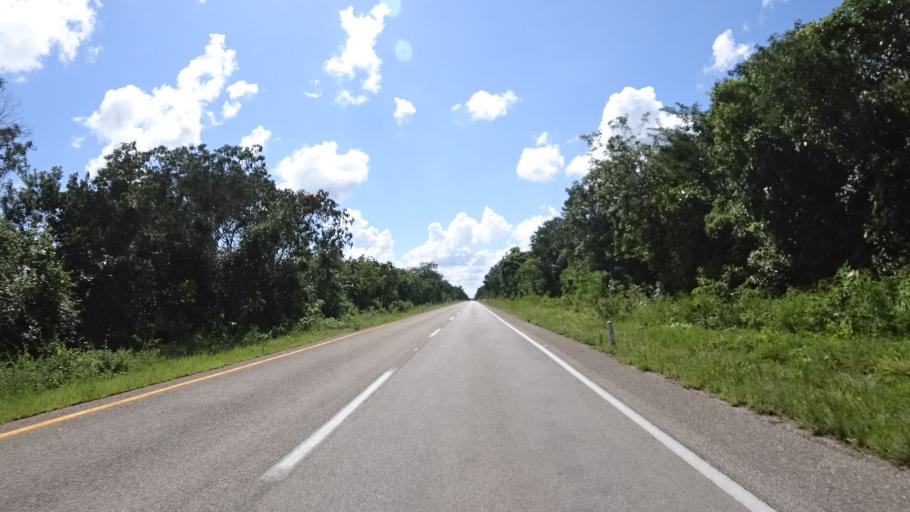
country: MX
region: Yucatan
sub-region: Uayma
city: Uayma
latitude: 20.7432
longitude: -88.2795
